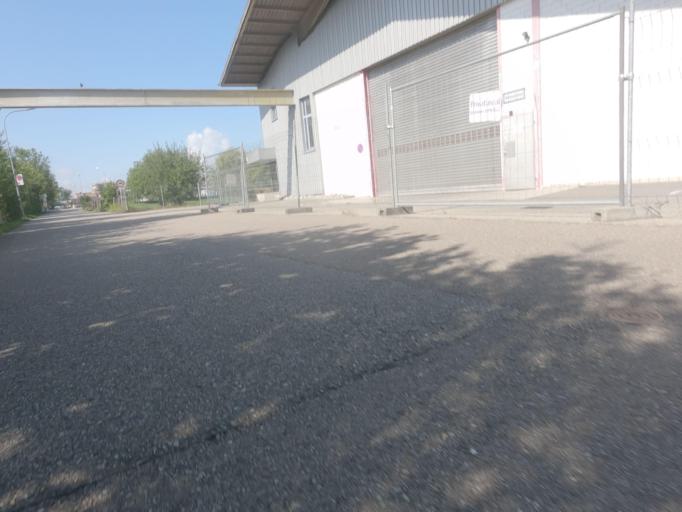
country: CH
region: Solothurn
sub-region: Bezirk Olten
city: Wangen
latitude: 47.3420
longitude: 7.8725
